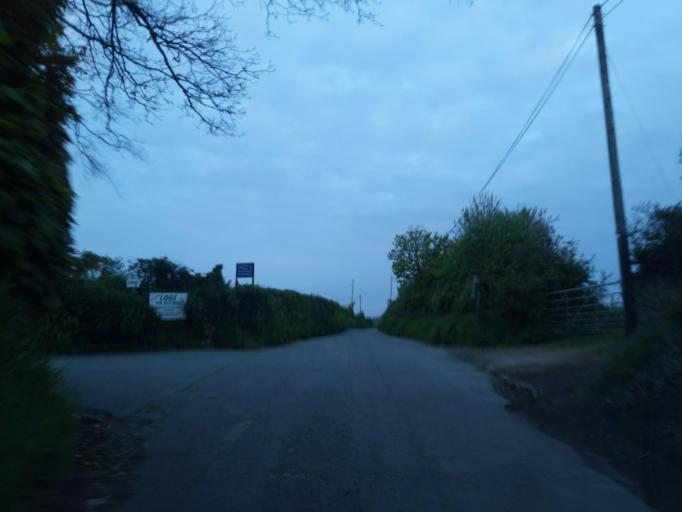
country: GB
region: England
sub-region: Cornwall
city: Polzeath
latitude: 50.5593
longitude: -4.8821
